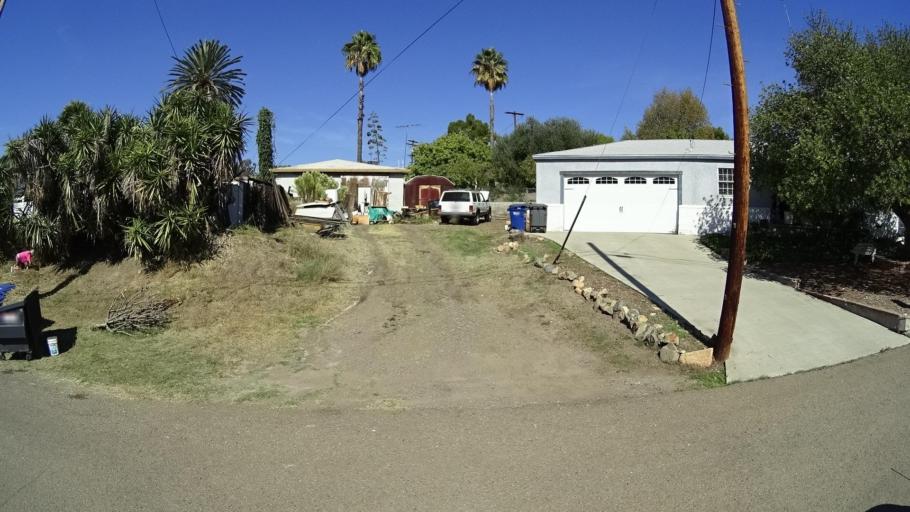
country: US
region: California
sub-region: San Diego County
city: Casa de Oro-Mount Helix
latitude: 32.7466
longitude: -116.9785
